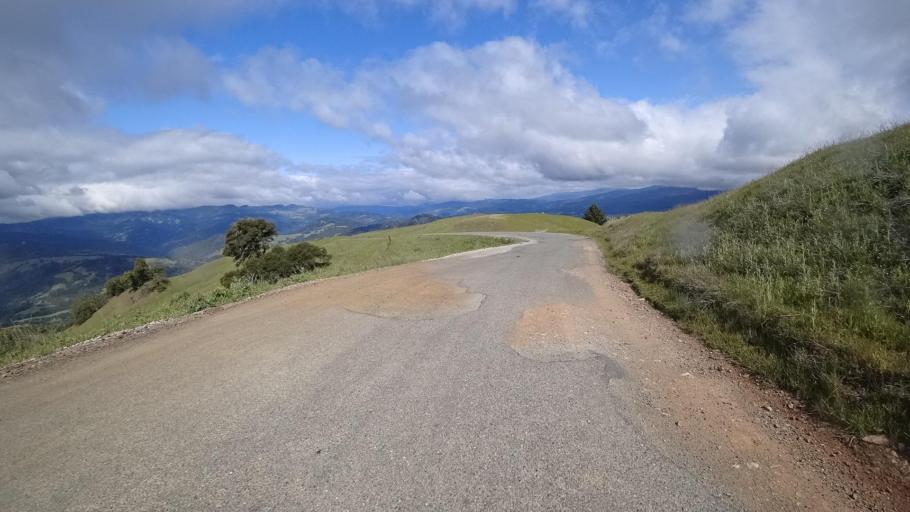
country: US
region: California
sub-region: Humboldt County
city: Redway
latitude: 40.1604
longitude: -123.5629
